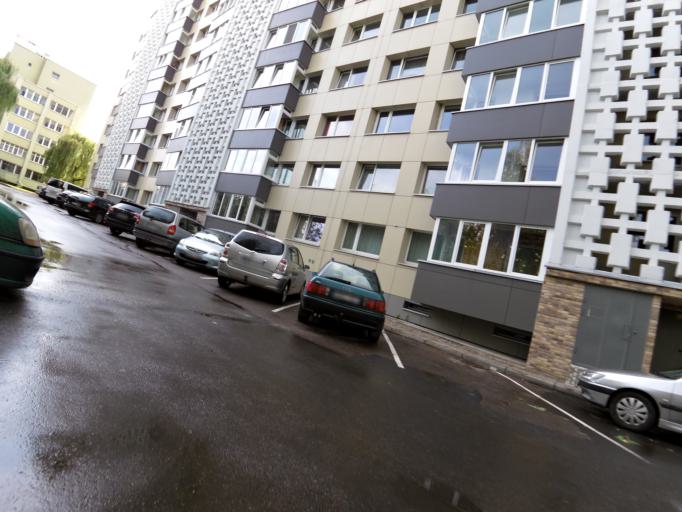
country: LT
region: Vilnius County
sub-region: Vilnius
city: Vilnius
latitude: 54.6972
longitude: 25.2923
